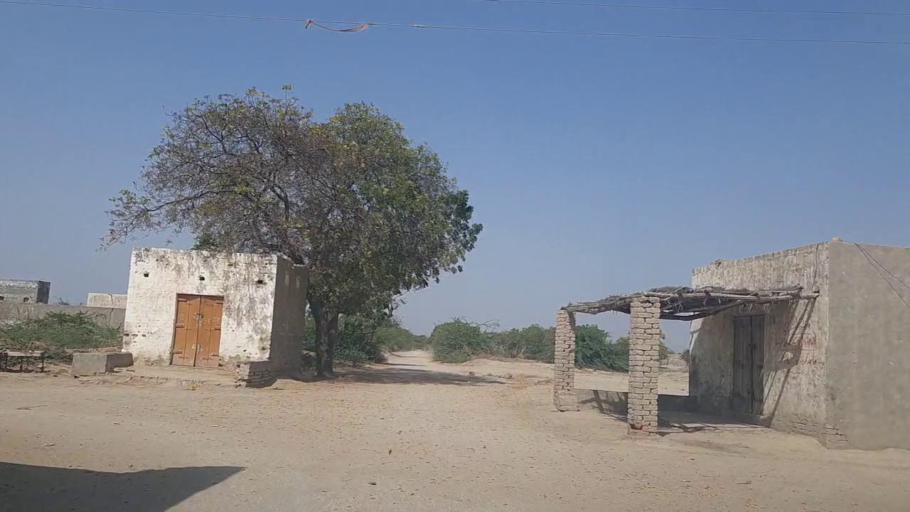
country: PK
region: Sindh
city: Naukot
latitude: 24.8484
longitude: 69.4395
